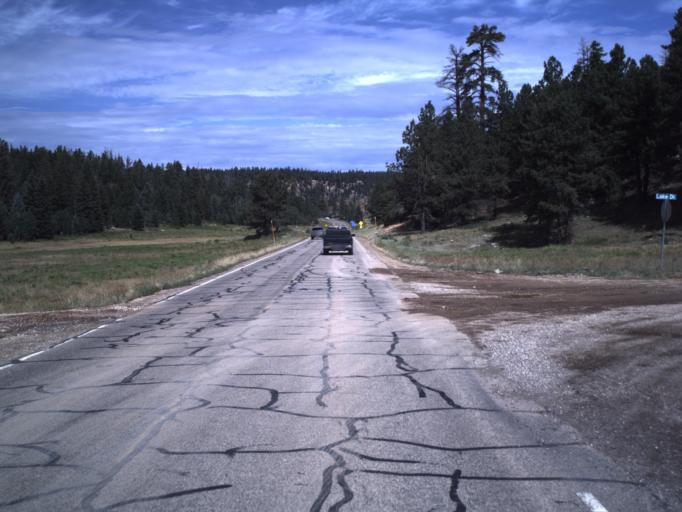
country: US
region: Utah
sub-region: Iron County
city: Parowan
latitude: 37.5215
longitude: -112.6540
